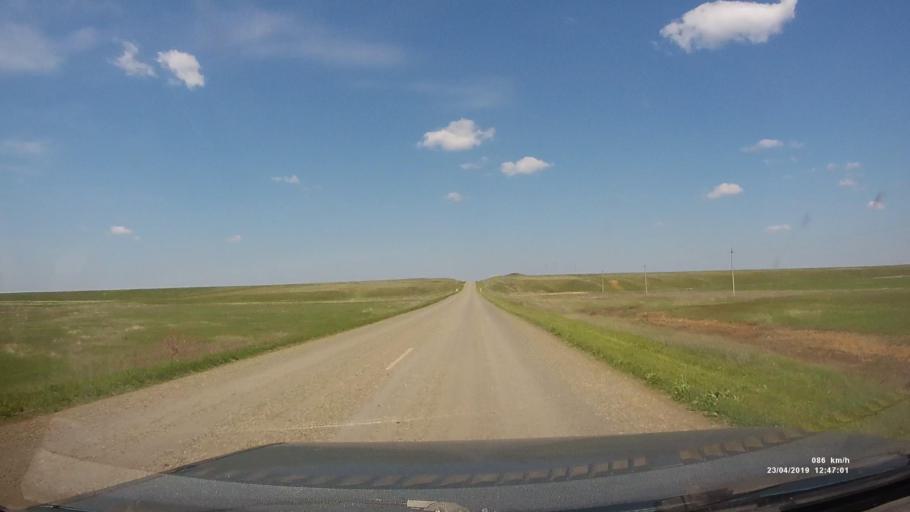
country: RU
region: Kalmykiya
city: Yashalta
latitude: 46.5070
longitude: 42.6385
